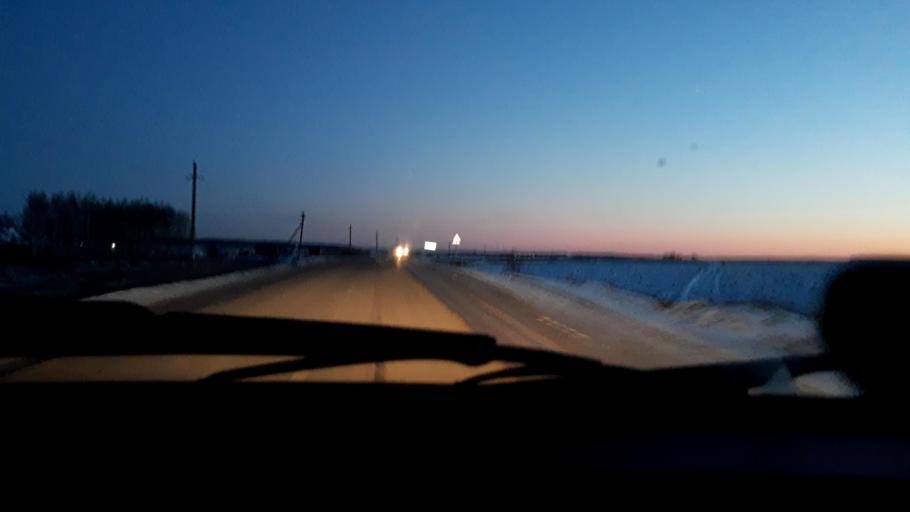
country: RU
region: Bashkortostan
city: Iglino
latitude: 54.7548
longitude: 56.3992
